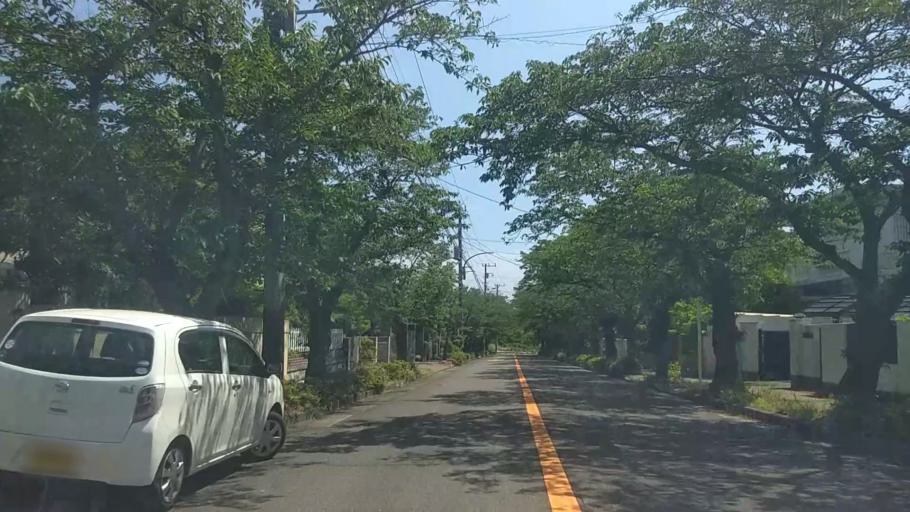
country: JP
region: Kanagawa
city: Zushi
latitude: 35.3133
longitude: 139.5769
